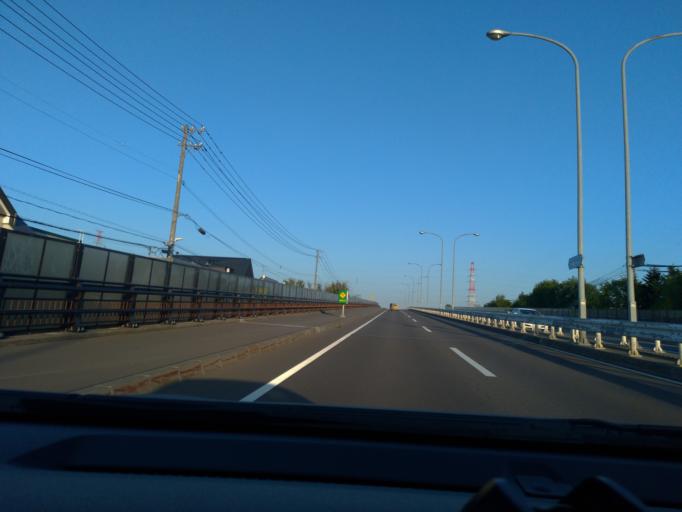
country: JP
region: Hokkaido
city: Ishikari
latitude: 43.1575
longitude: 141.4058
